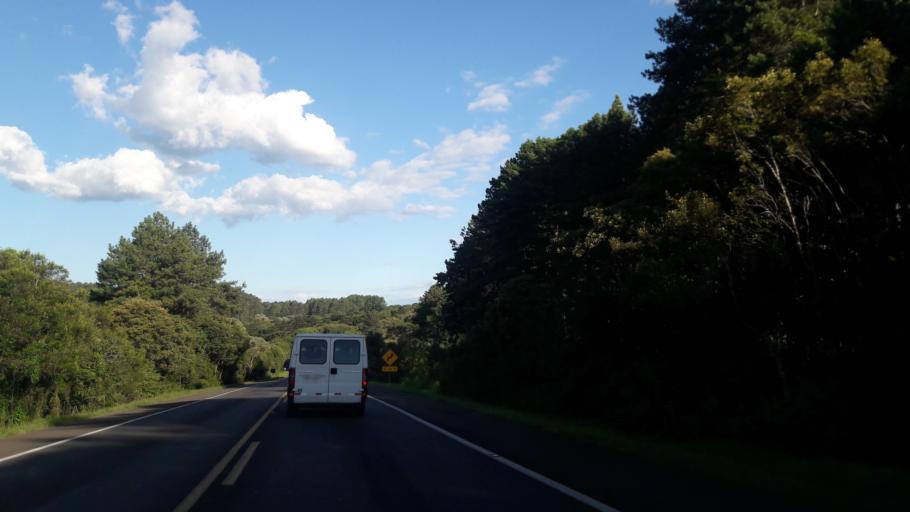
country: BR
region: Parana
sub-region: Guarapuava
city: Guarapuava
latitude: -25.3697
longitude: -51.3265
